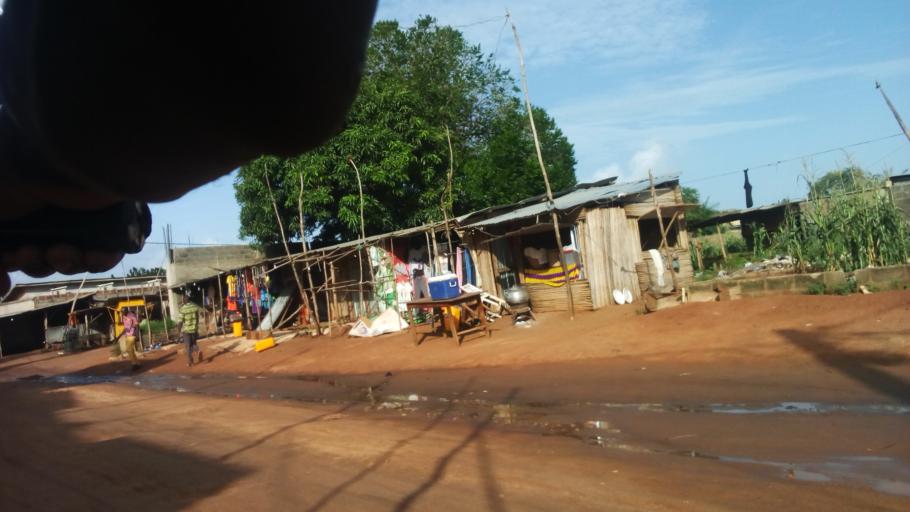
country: BJ
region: Atlantique
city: Abomey-Calavi
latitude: 6.4279
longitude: 2.3399
